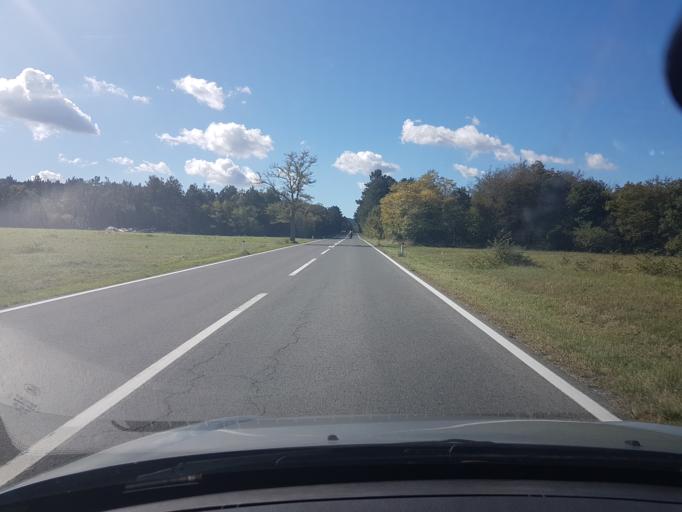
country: SI
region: Sezana
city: Sezana
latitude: 45.7333
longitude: 13.9209
